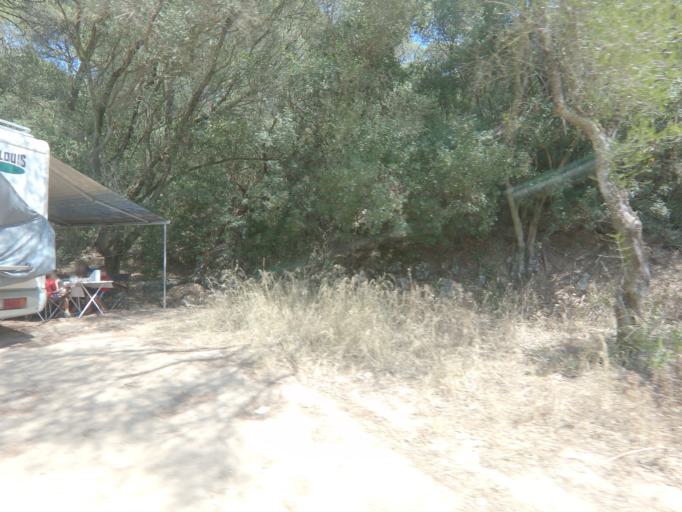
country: PT
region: Setubal
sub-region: Setubal
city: Setubal
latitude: 38.5128
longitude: -8.9296
